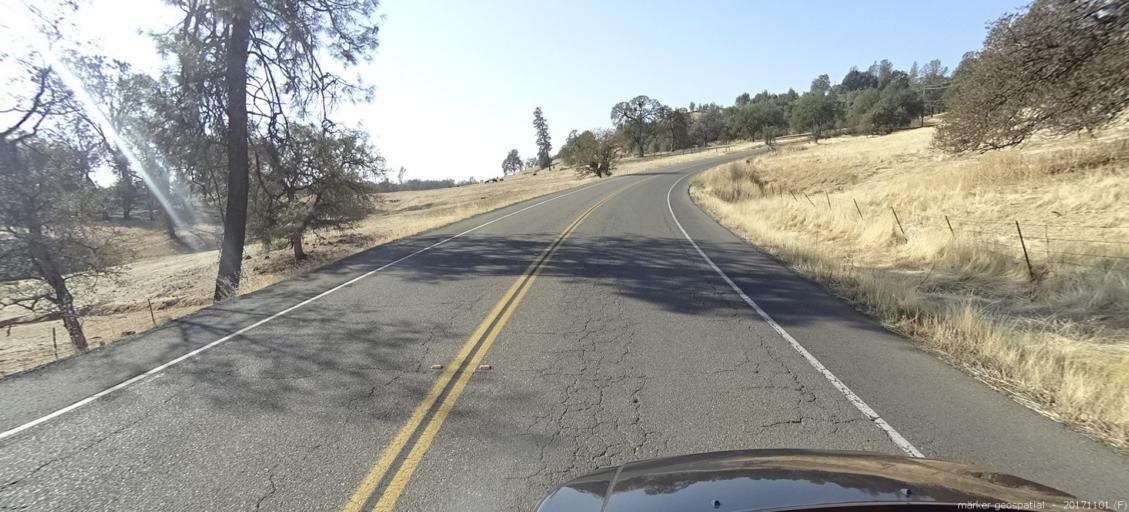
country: US
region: California
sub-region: Shasta County
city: Shasta Lake
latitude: 40.6858
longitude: -122.3295
